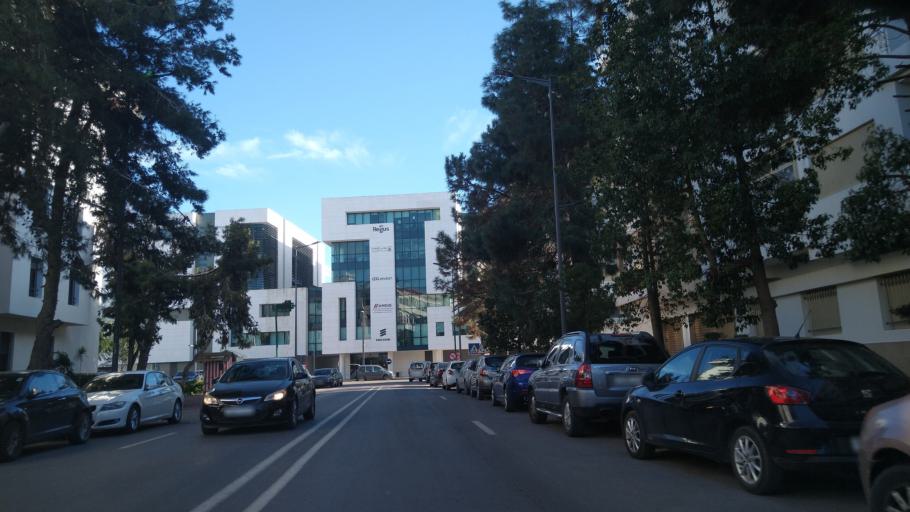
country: MA
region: Rabat-Sale-Zemmour-Zaer
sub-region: Skhirate-Temara
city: Temara
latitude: 33.9630
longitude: -6.8673
